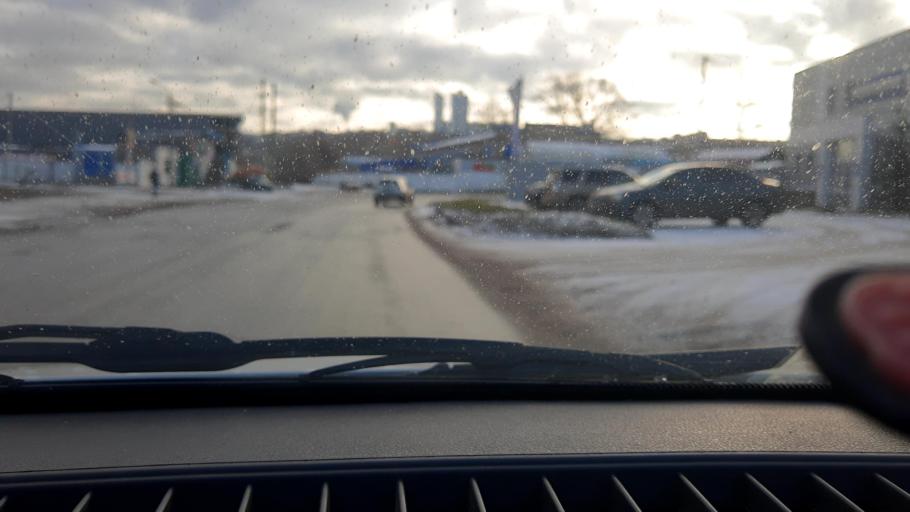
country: RU
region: Bashkortostan
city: Ufa
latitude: 54.7448
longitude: 55.9226
